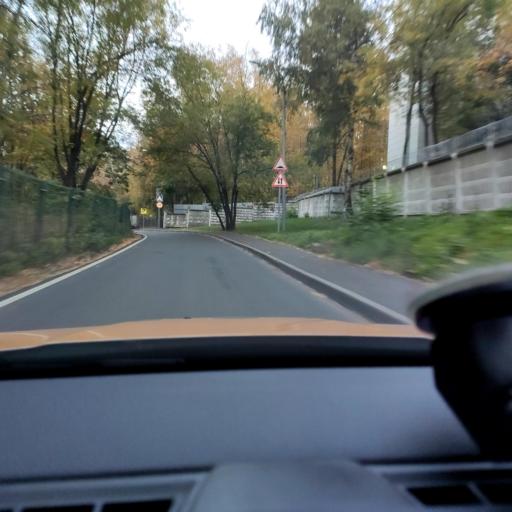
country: RU
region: Moscow
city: Vatutino
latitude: 55.8619
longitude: 37.7012
